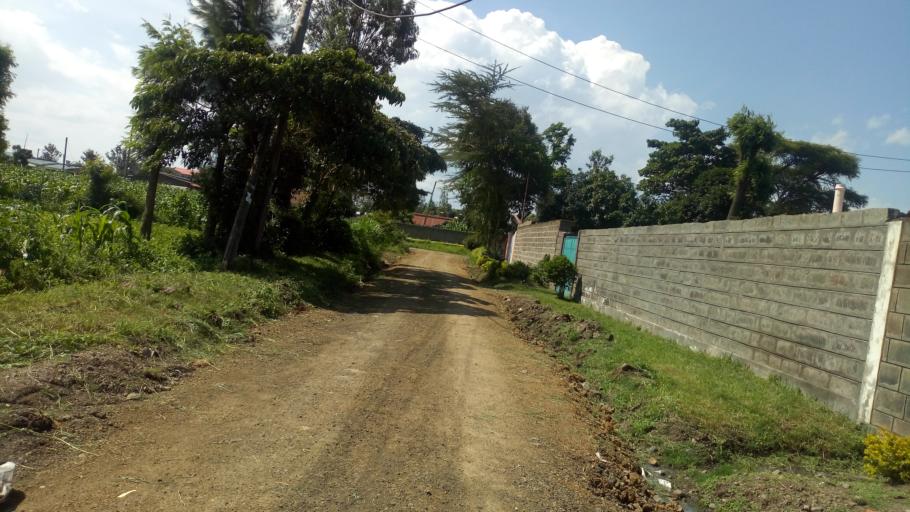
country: KE
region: Nakuru
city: Nakuru
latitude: -0.2767
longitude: 36.1196
